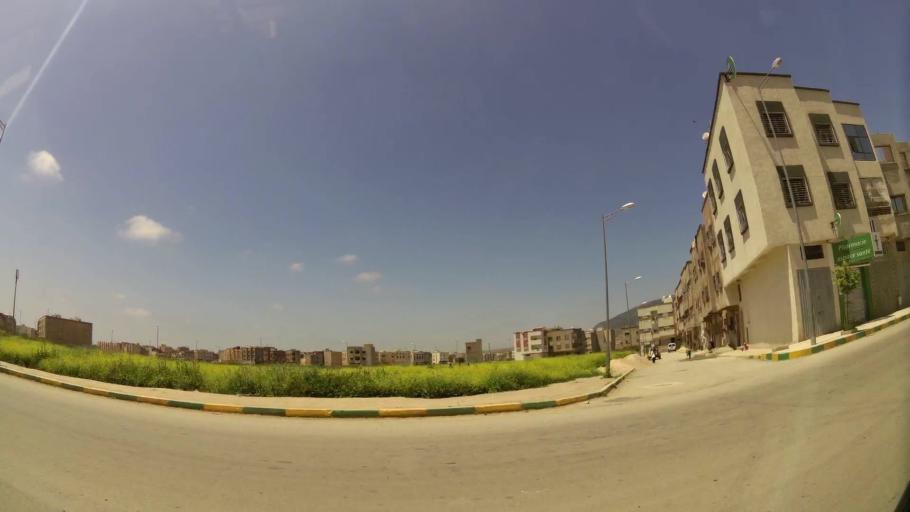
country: MA
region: Fes-Boulemane
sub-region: Fes
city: Fes
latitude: 34.0339
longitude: -5.0437
